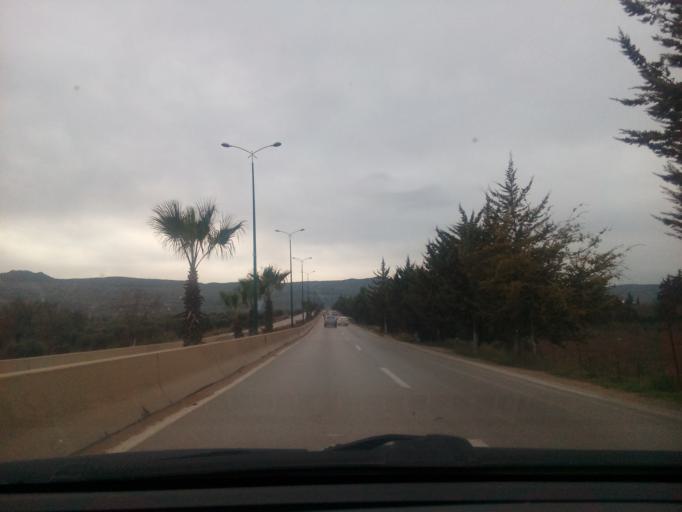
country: DZ
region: Tlemcen
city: Mansoura
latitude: 34.8767
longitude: -1.3491
